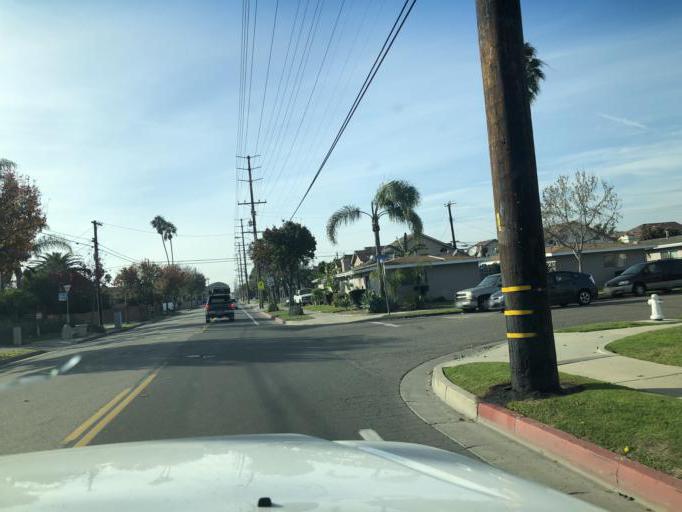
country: US
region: California
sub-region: Orange County
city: Costa Mesa
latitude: 33.6561
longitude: -117.9281
